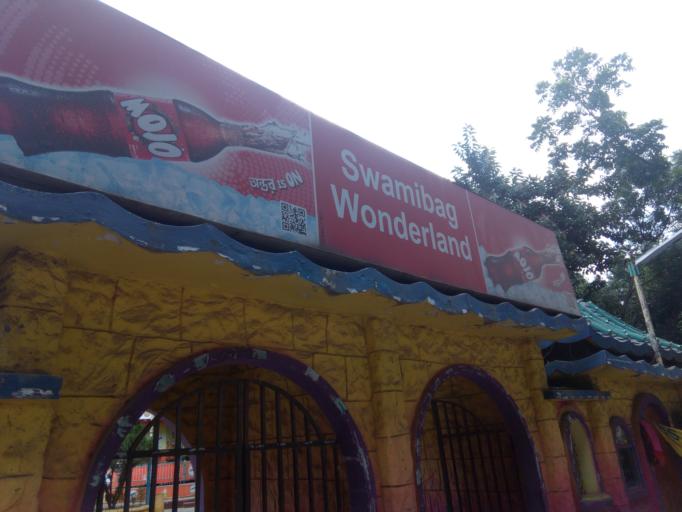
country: BD
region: Dhaka
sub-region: Dhaka
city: Dhaka
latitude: 23.7150
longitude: 90.4246
